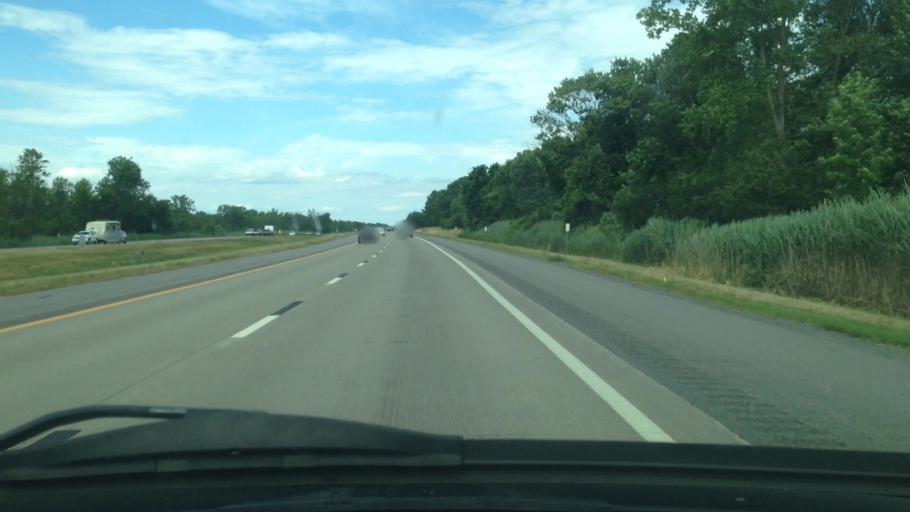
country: US
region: New York
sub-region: Onondaga County
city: Jordan
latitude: 43.0805
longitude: -76.4595
